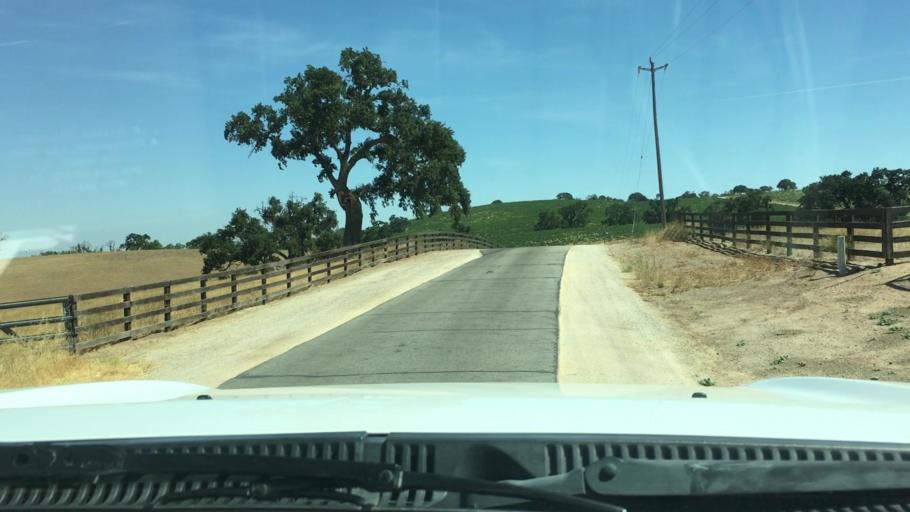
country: US
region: California
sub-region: San Luis Obispo County
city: Paso Robles
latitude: 35.5756
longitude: -120.6030
